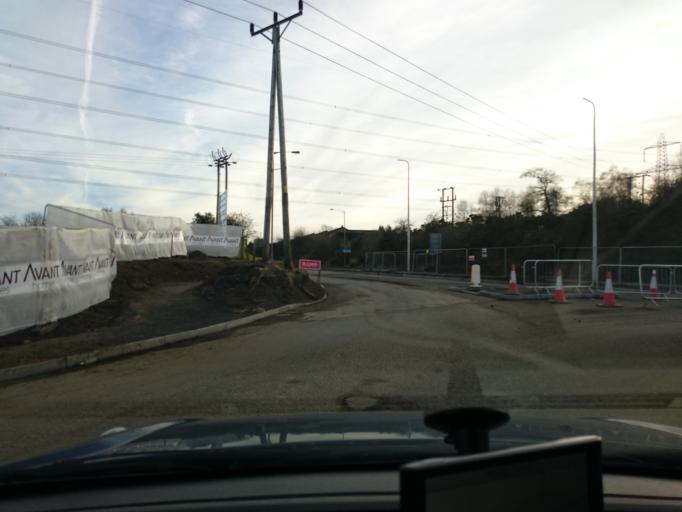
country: GB
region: Scotland
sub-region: Falkirk
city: Denny
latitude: 56.0123
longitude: -3.9061
